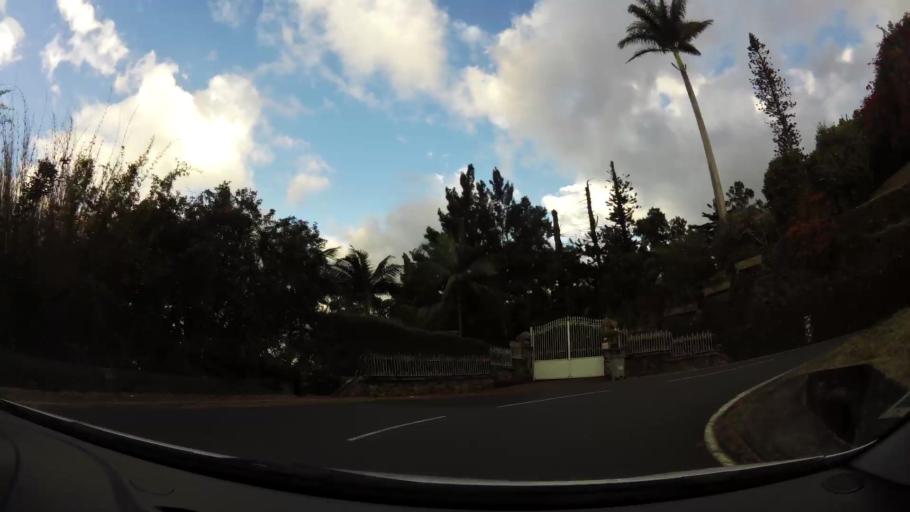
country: RE
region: Reunion
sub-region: Reunion
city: Saint-Denis
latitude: -20.9098
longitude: 55.4433
